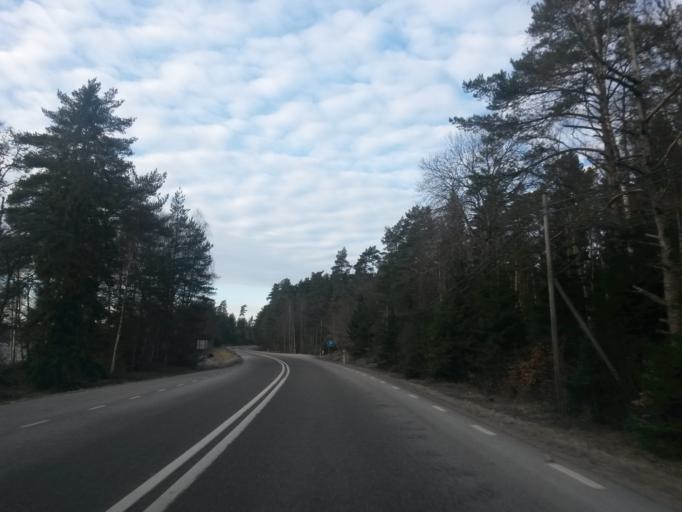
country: SE
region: Vaestra Goetaland
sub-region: Vargarda Kommun
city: Vargarda
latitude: 57.9421
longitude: 12.8452
